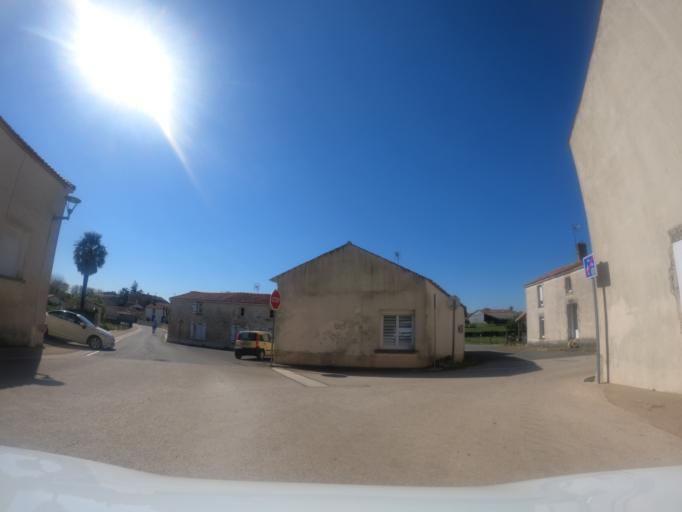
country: FR
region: Pays de la Loire
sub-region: Departement de la Vendee
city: Fontenay-le-Comte
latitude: 46.4238
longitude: -0.8162
